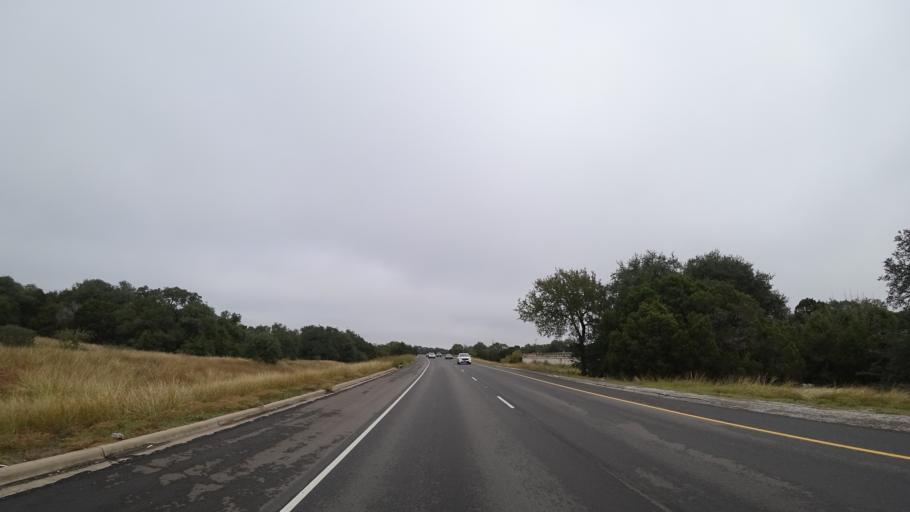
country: US
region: Texas
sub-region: Travis County
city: Shady Hollow
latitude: 30.1950
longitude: -97.8702
